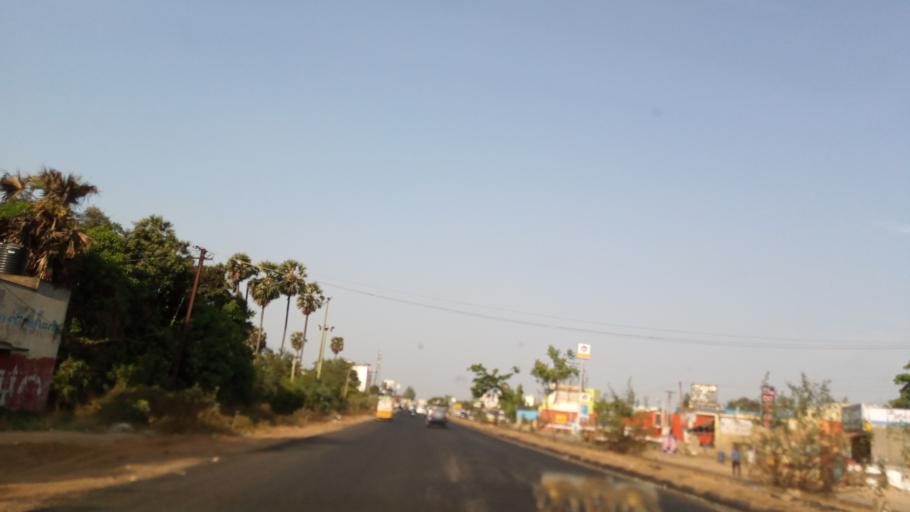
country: IN
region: Tamil Nadu
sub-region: Kancheepuram
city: Nandambakkam
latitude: 13.0310
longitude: 80.0344
